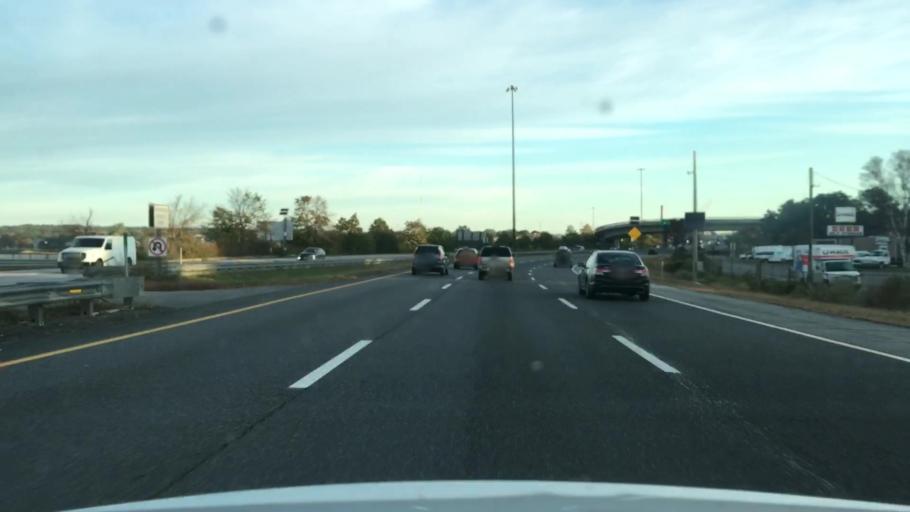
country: US
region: Maine
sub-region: Cumberland County
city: Portland
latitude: 43.6706
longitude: -70.2584
